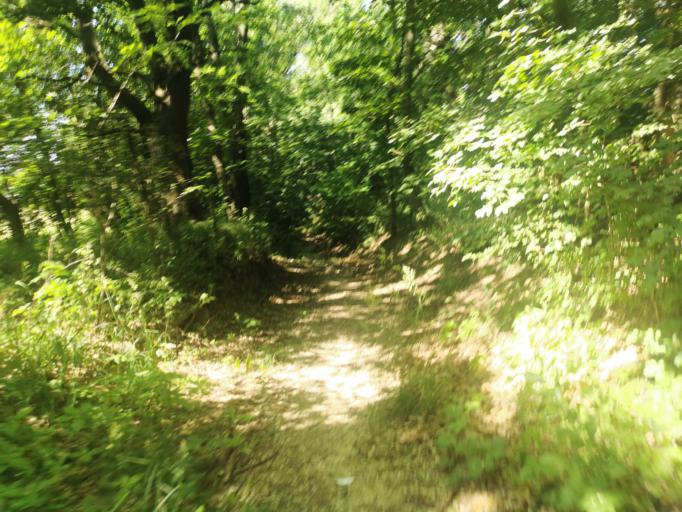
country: SK
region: Trnavsky
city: Smolenice
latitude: 48.5498
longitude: 17.3570
